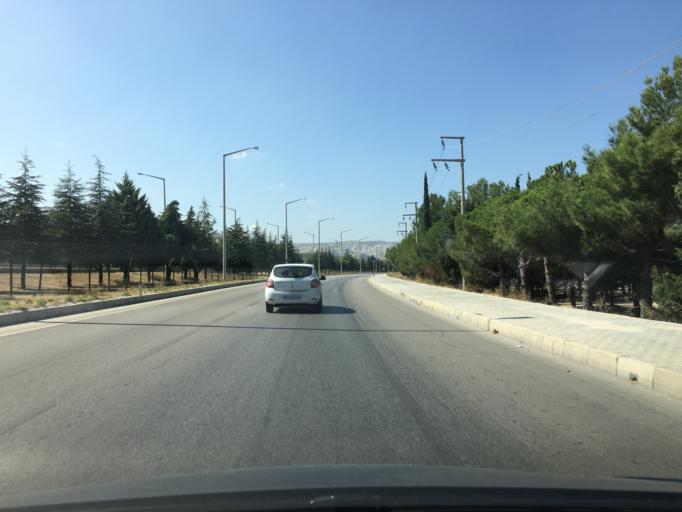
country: TR
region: Burdur
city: Burdur
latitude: 37.7333
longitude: 30.3092
